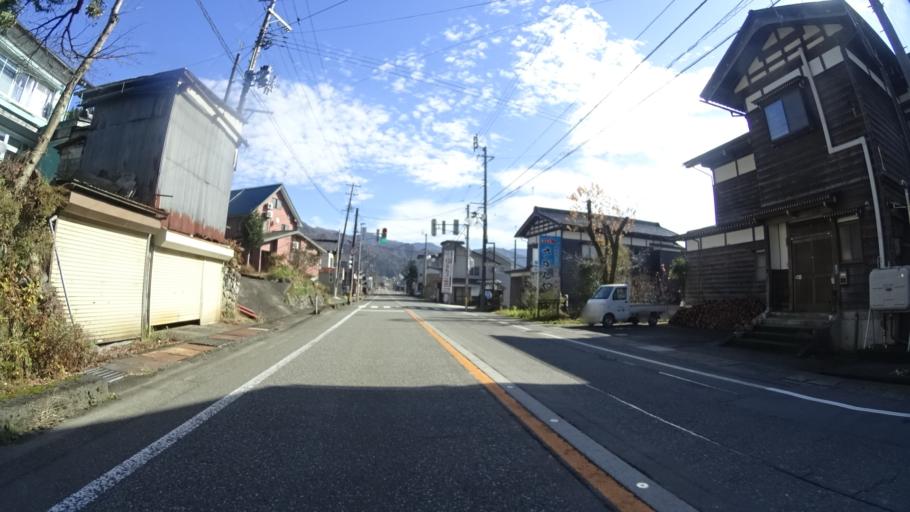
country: JP
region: Niigata
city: Muikamachi
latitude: 37.2083
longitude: 139.0617
